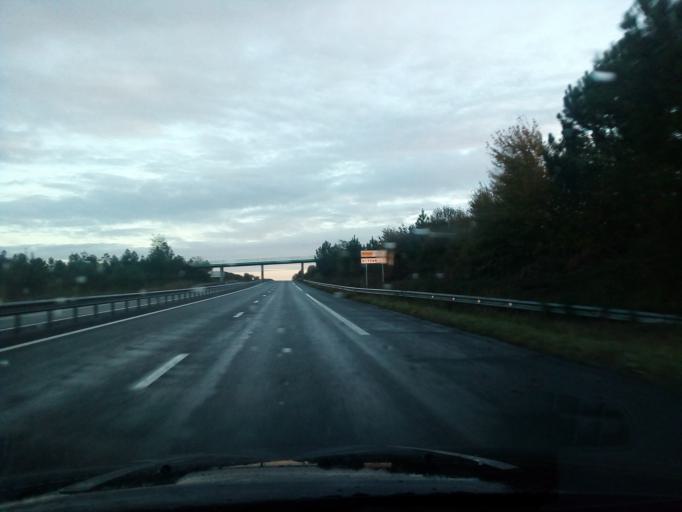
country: FR
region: Aquitaine
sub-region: Departement de la Gironde
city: Saint-Mariens
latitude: 45.1368
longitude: -0.3691
